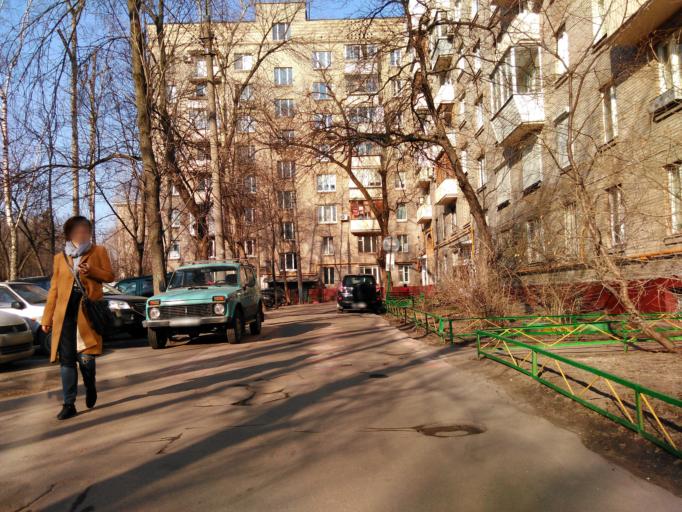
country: RU
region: Moscow
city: Ramenki
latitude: 55.7081
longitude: 37.5139
